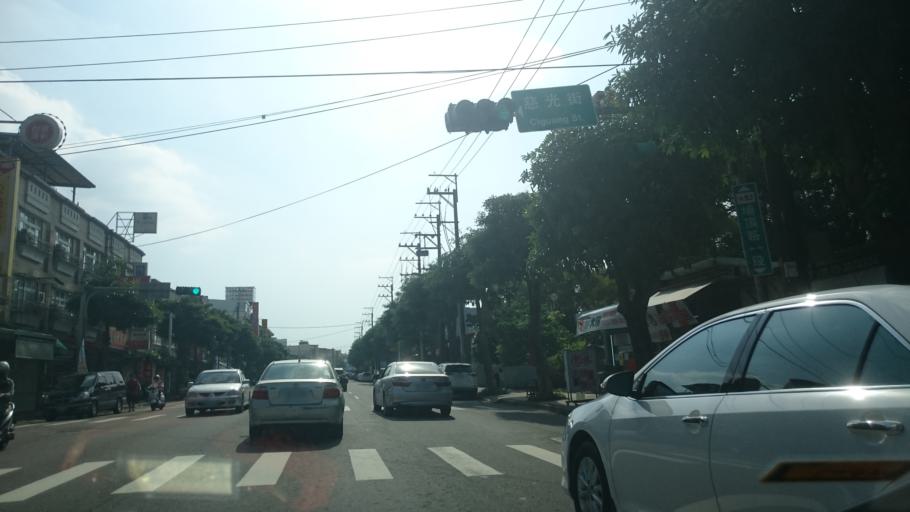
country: TW
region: Taiwan
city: Daxi
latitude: 24.9053
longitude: 121.2769
